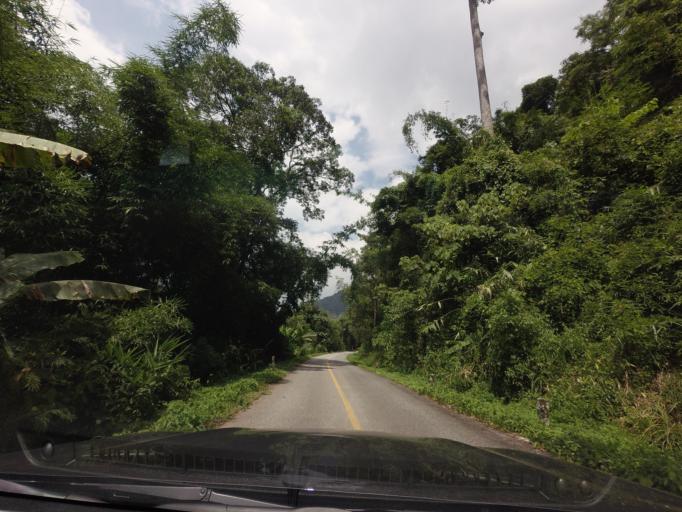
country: TH
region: Loei
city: Na Haeo
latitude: 17.6991
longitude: 100.9471
